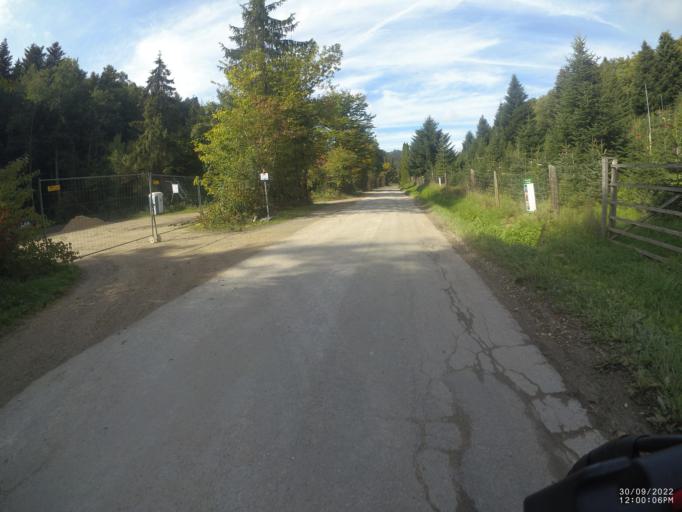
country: DE
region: Baden-Wuerttemberg
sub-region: Regierungsbezirk Stuttgart
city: Wangen
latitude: 48.7477
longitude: 9.6111
